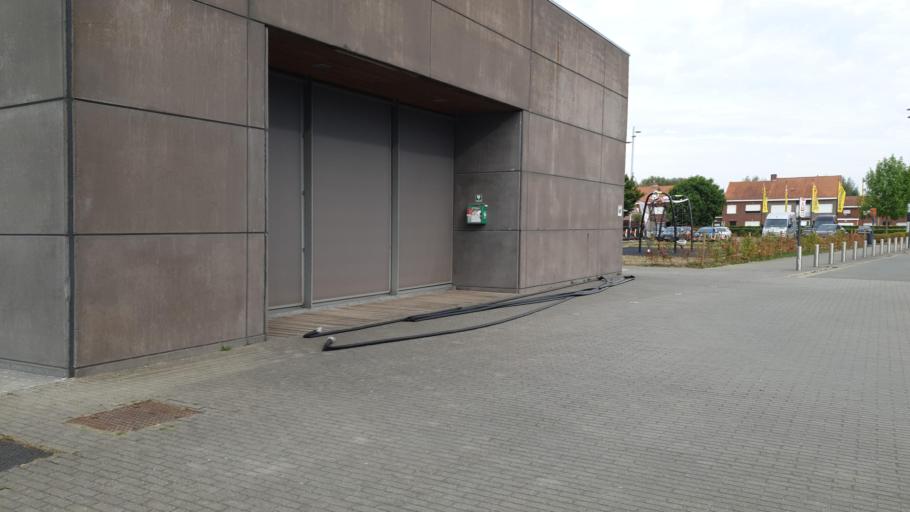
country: BE
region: Flanders
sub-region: Provincie West-Vlaanderen
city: Ieper
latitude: 50.9100
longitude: 2.9165
